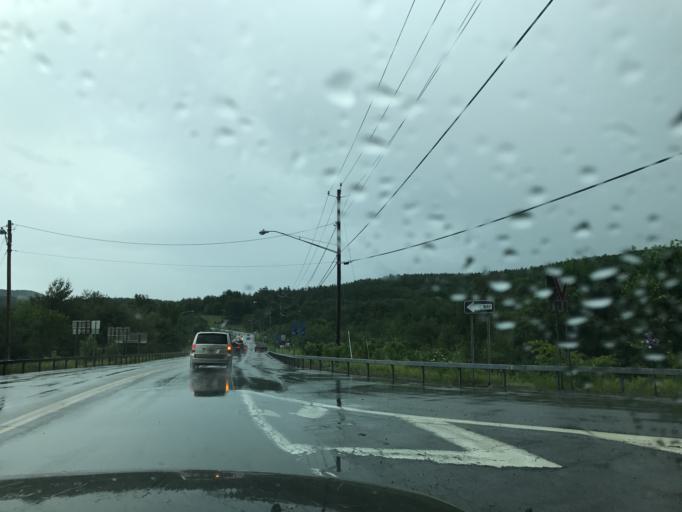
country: US
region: New York
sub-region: Warren County
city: Warrensburg
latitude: 43.4864
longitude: -73.7566
